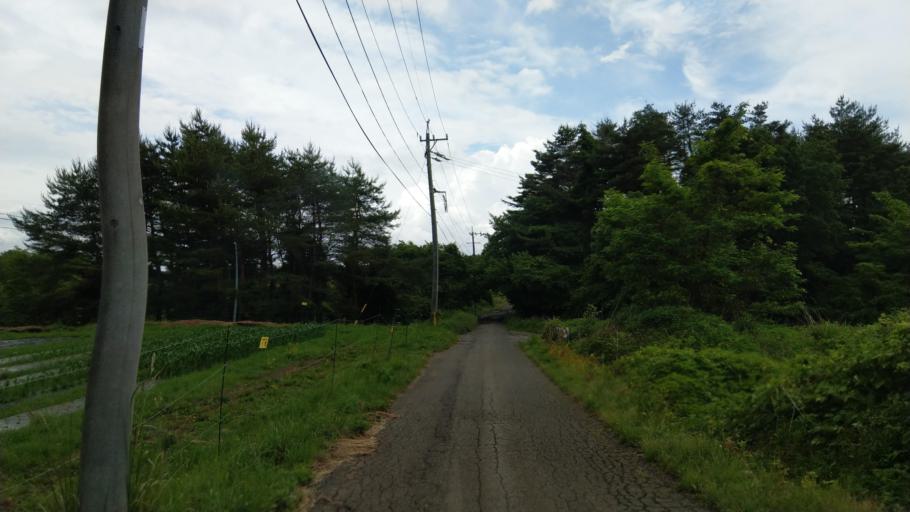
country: JP
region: Nagano
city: Komoro
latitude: 36.2863
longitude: 138.3756
